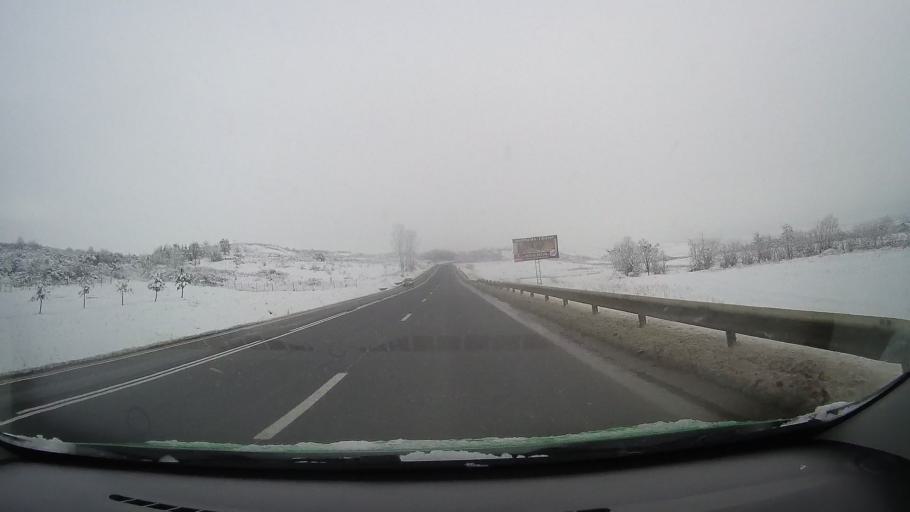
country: RO
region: Sibiu
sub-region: Comuna Cristian
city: Cristian
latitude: 45.7887
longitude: 24.0523
